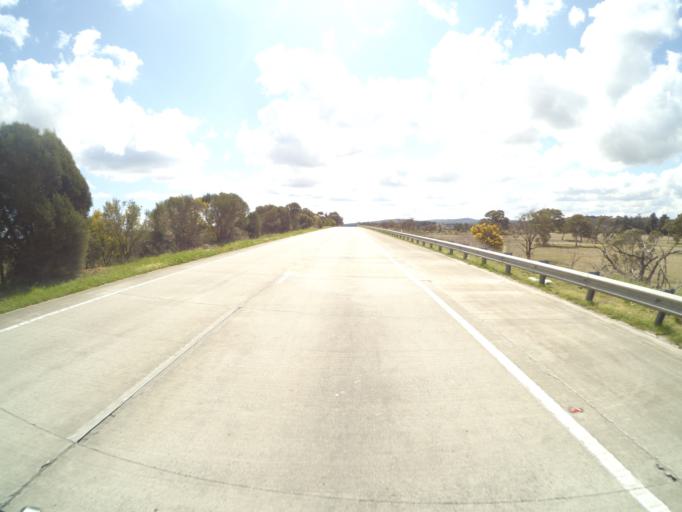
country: AU
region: New South Wales
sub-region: Wingecarribee
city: Moss Vale
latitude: -34.5000
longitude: 150.3106
